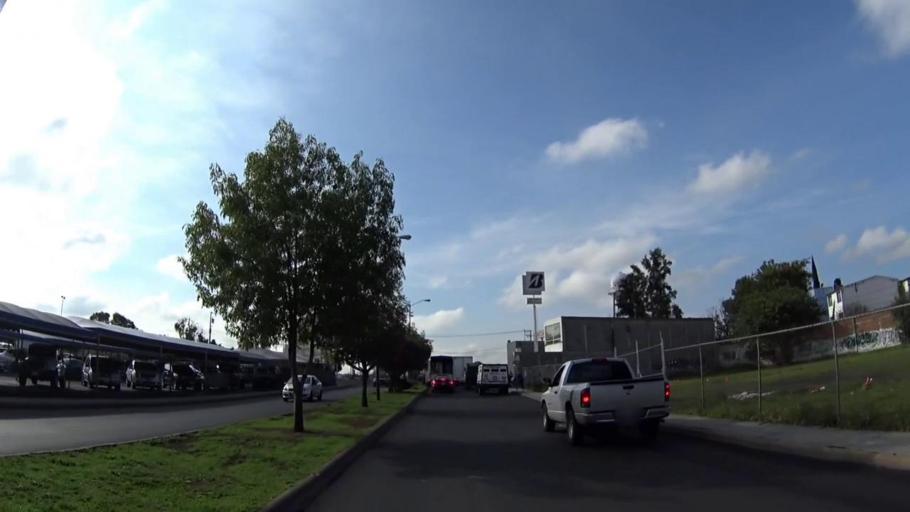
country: MX
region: Michoacan
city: Morelia
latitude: 19.6929
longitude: -101.2130
